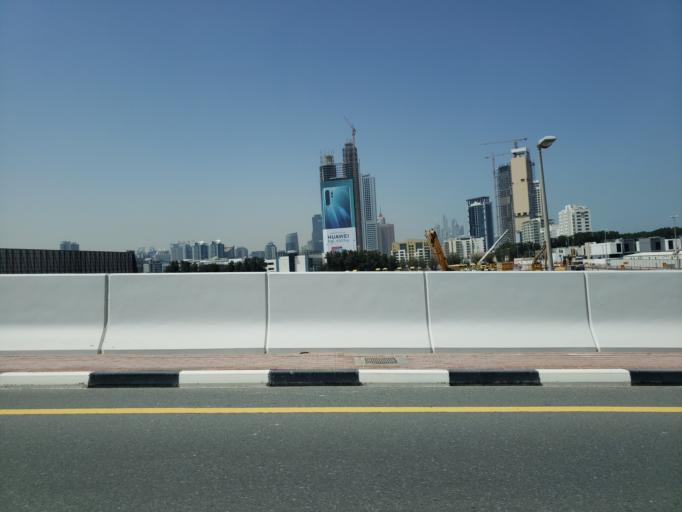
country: AE
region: Dubai
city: Dubai
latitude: 25.1148
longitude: 55.1857
